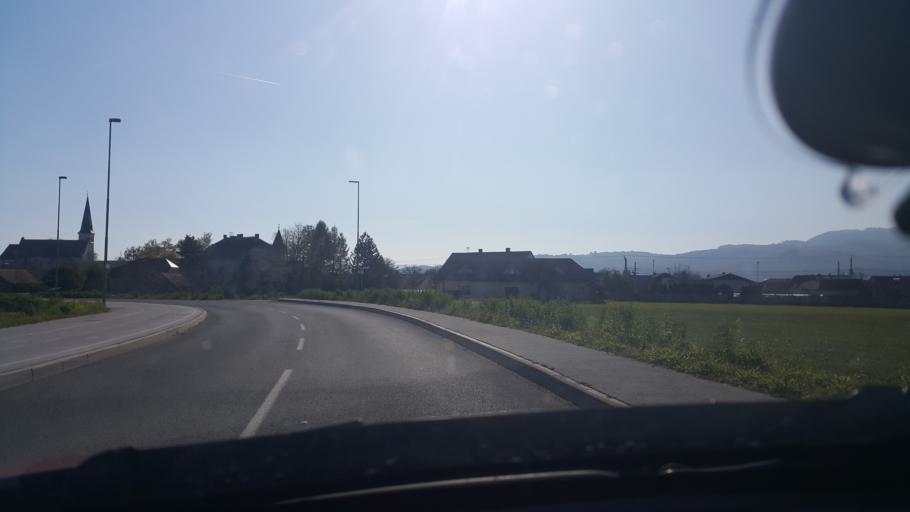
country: HR
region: Zagrebacka
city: Bregana
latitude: 45.8987
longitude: 15.6599
